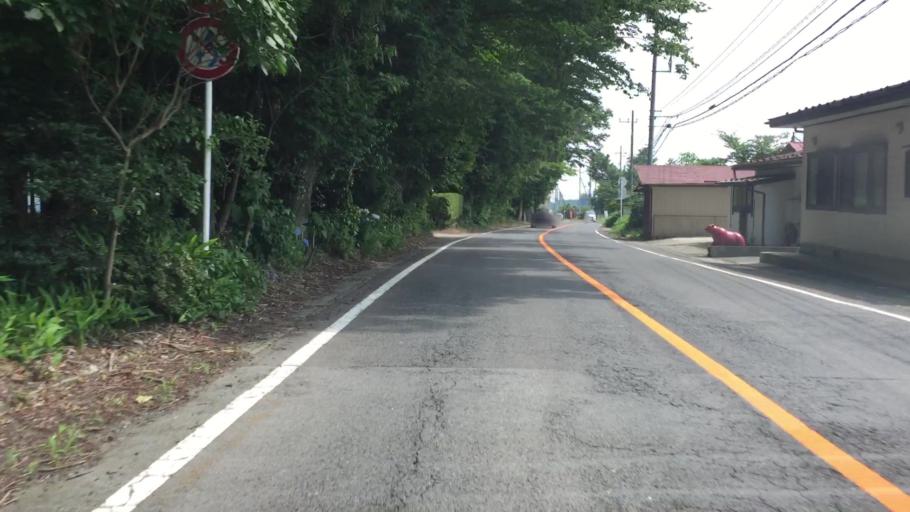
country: JP
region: Tochigi
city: Kuroiso
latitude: 37.0335
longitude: 139.9434
